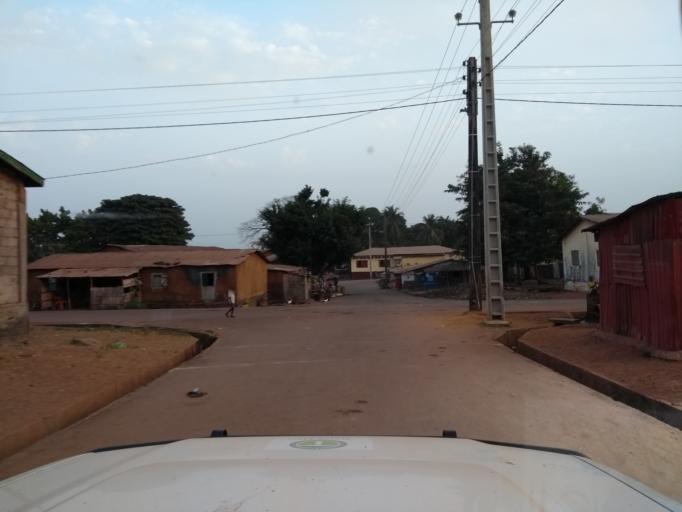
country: GN
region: Kindia
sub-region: Prefecture de Dubreka
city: Dubreka
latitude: 9.7897
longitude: -13.5240
